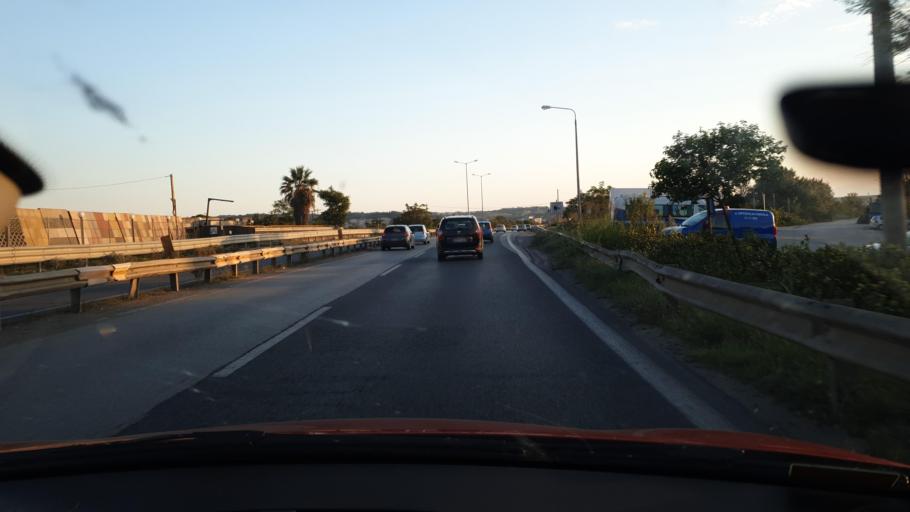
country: GR
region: Central Macedonia
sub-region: Nomos Thessalonikis
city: Neo Rysi
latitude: 40.5201
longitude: 22.9942
